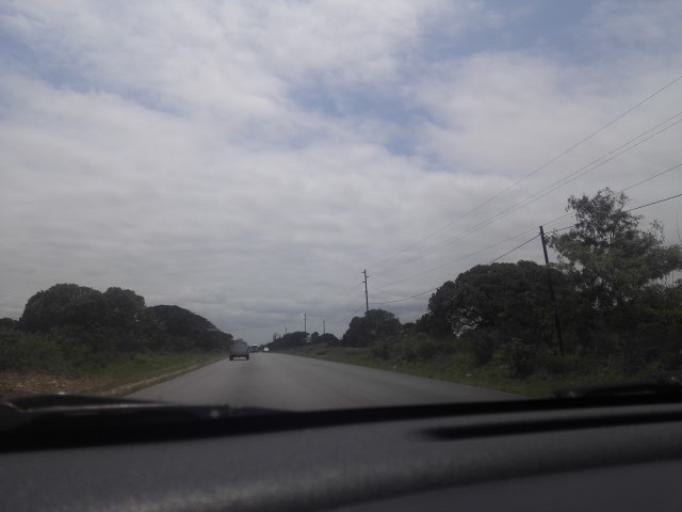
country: MZ
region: Maputo
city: Manhica
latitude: -25.4106
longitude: 32.7527
